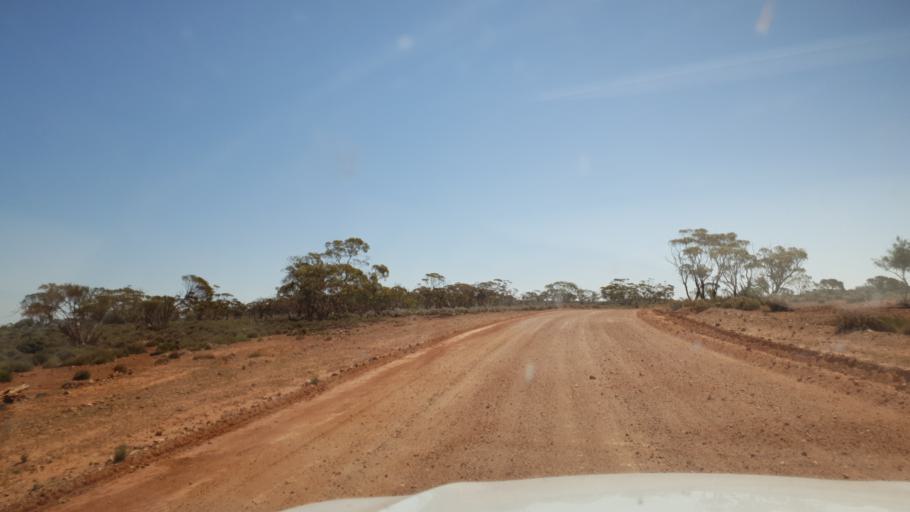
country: AU
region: South Australia
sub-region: Whyalla
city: Whyalla
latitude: -32.6193
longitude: 136.7680
